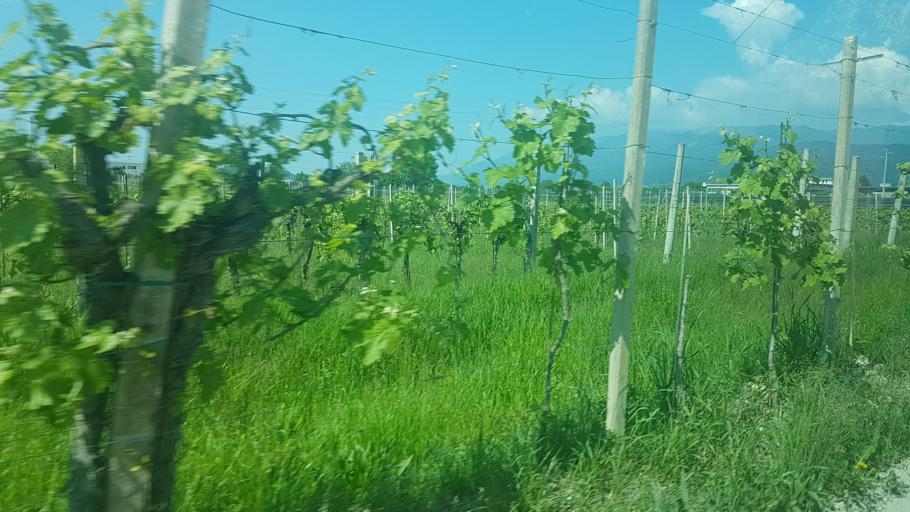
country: IT
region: Veneto
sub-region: Provincia di Treviso
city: Bigolino
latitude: 45.8778
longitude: 12.0136
